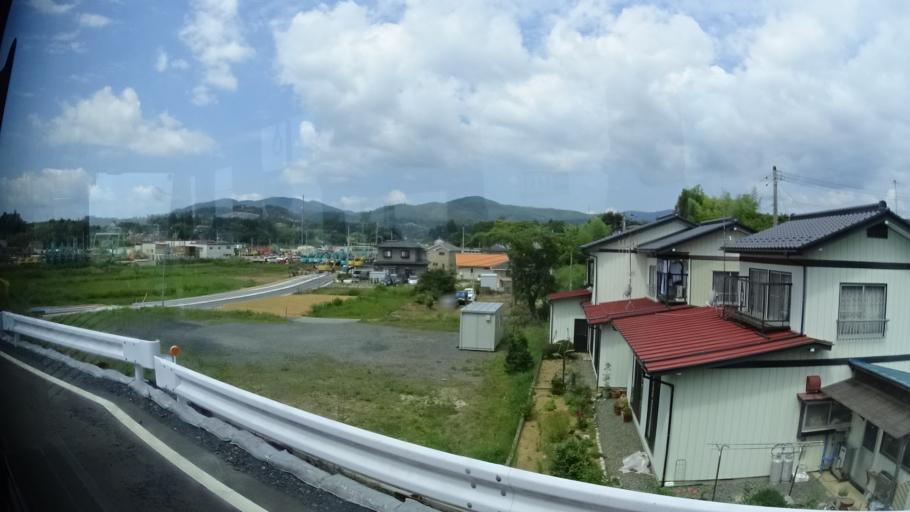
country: JP
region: Iwate
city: Ofunato
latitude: 38.8580
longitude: 141.5826
